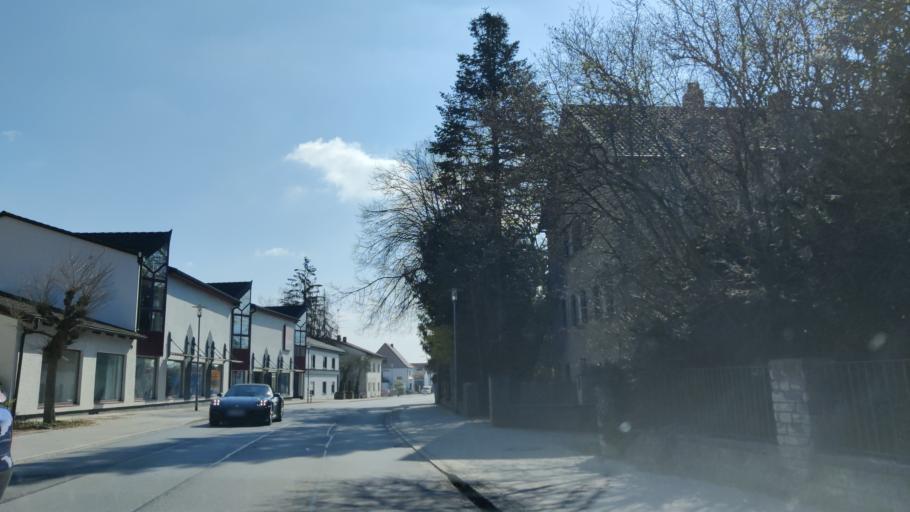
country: DE
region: Bavaria
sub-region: Lower Bavaria
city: Strasskirchen
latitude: 48.8331
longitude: 12.7168
